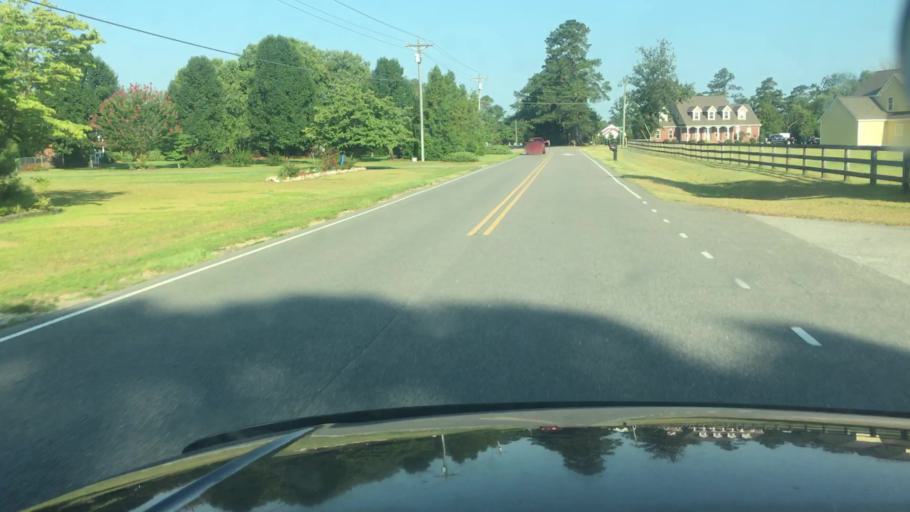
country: US
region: North Carolina
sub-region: Robeson County
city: Saint Pauls
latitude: 34.8490
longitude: -78.8640
